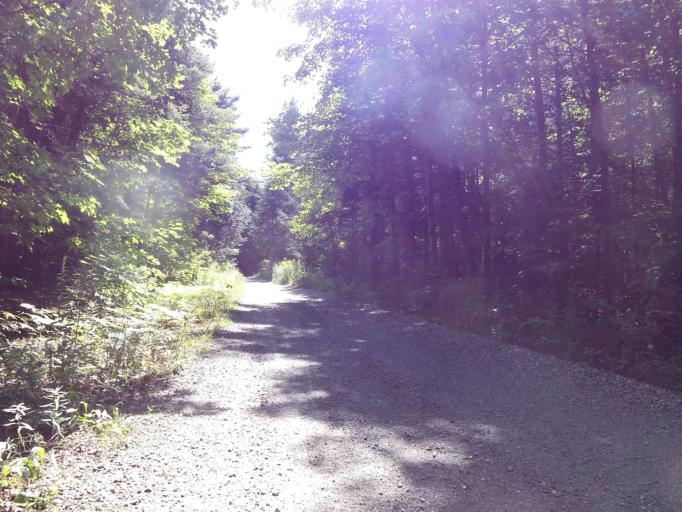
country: CA
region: Ontario
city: Renfrew
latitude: 45.0242
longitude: -76.7047
